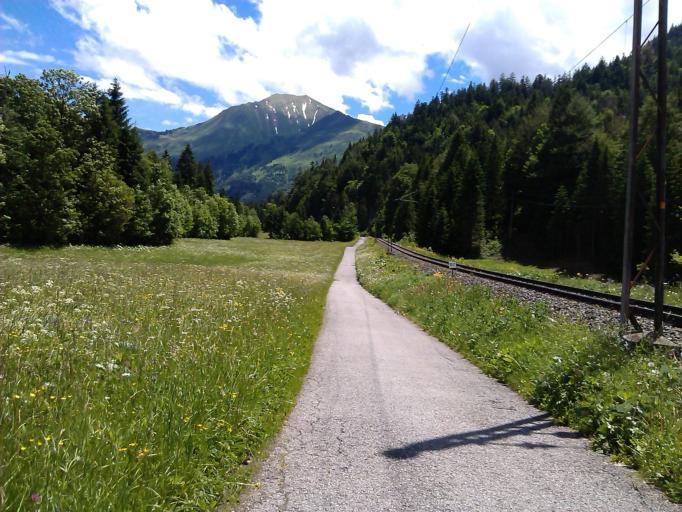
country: AT
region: Tyrol
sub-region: Politischer Bezirk Reutte
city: Bichlbach
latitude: 47.4321
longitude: 10.7671
